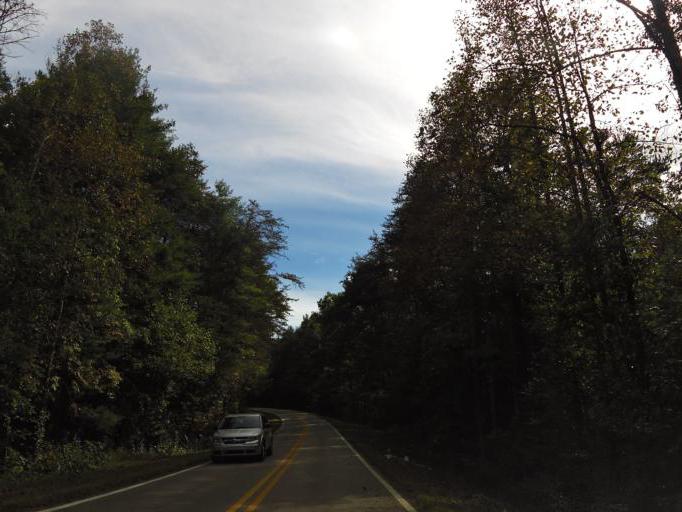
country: US
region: Georgia
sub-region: Pickens County
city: Nelson
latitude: 34.4974
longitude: -84.2693
